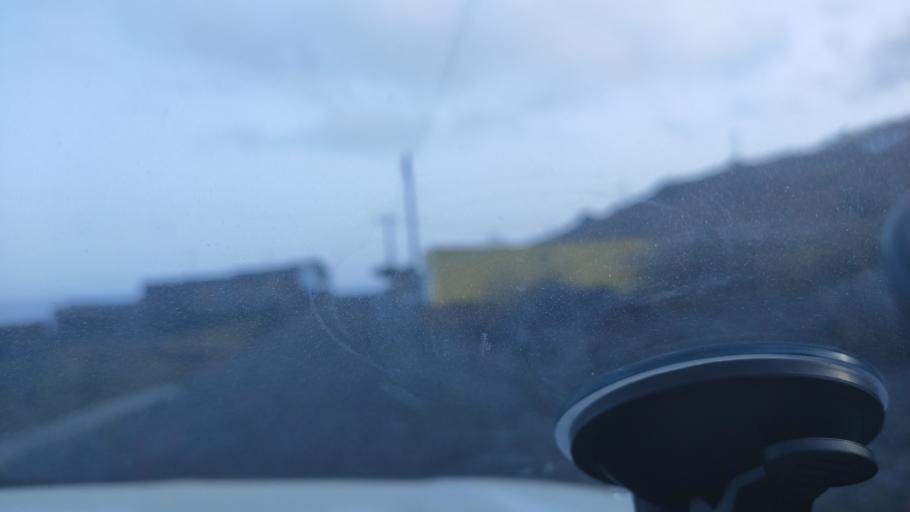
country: CV
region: Mosteiros
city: Porto dos Mosteiros
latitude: 15.0058
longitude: -24.3041
